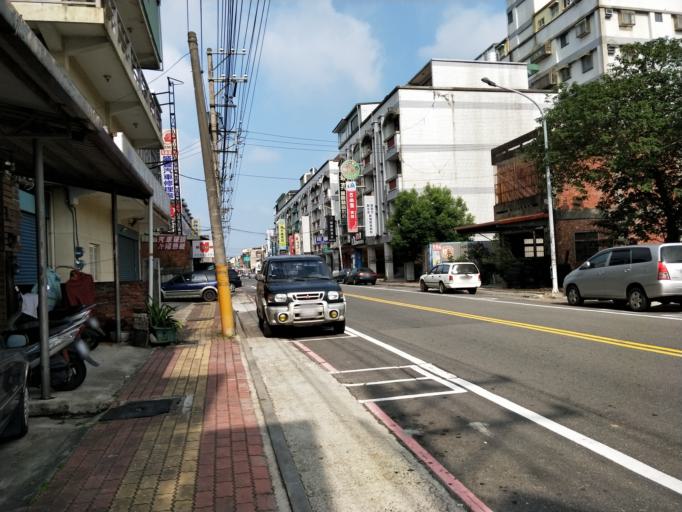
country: TW
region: Taiwan
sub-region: Hsinchu
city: Zhubei
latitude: 24.8266
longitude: 121.0843
